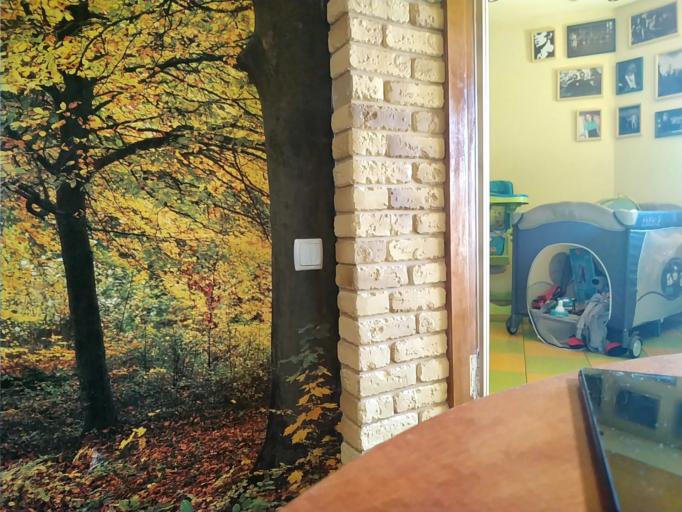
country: RU
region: Tverskaya
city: Krasnomayskiy
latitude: 57.6214
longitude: 34.4155
